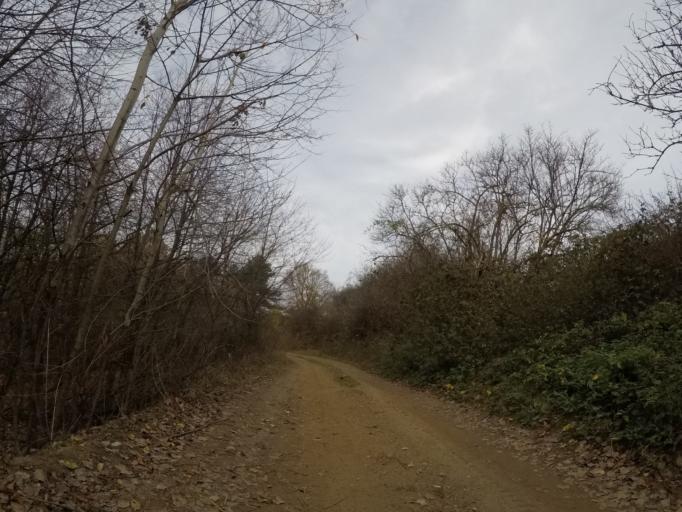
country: SK
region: Presovsky
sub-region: Okres Presov
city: Presov
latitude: 48.9241
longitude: 21.1439
